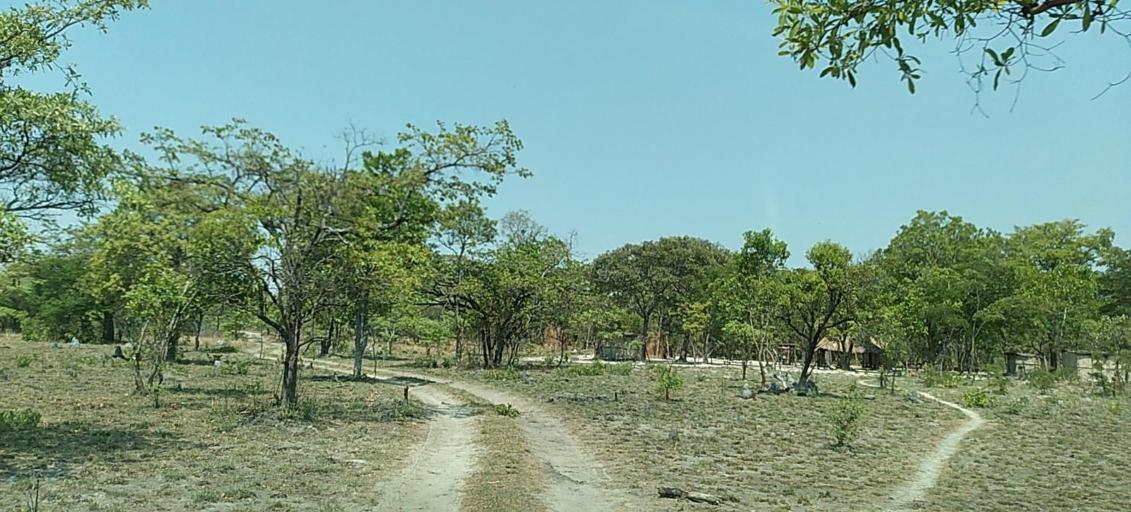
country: ZM
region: Copperbelt
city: Mpongwe
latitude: -13.8435
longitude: 28.0583
